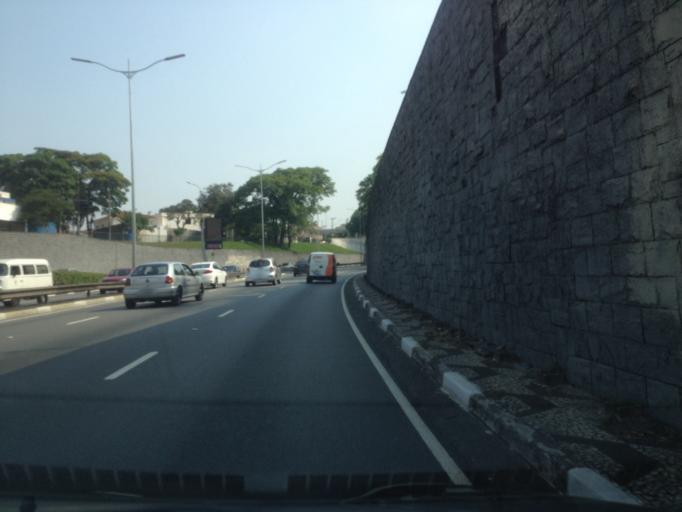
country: BR
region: Sao Paulo
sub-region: Sao Paulo
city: Sao Paulo
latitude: -23.6061
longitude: -46.6518
